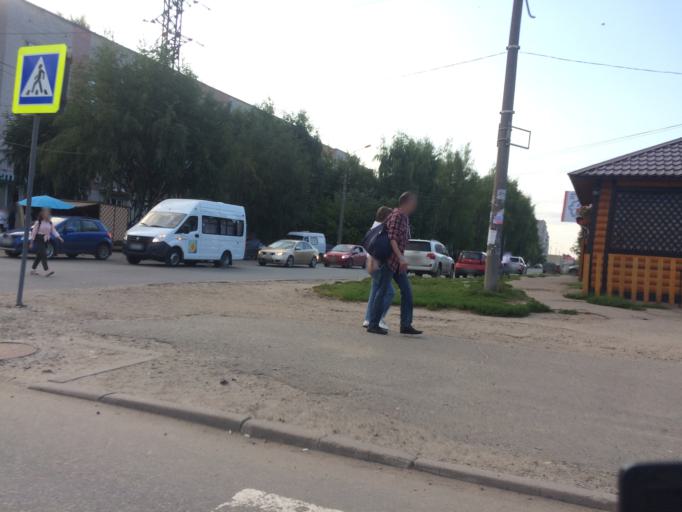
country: RU
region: Mariy-El
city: Medvedevo
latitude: 56.6416
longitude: 47.8452
